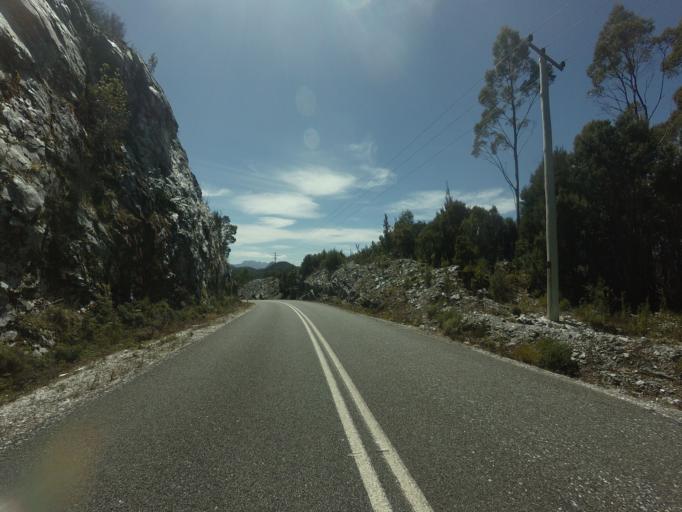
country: AU
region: Tasmania
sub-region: West Coast
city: Queenstown
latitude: -42.7580
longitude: 146.0030
